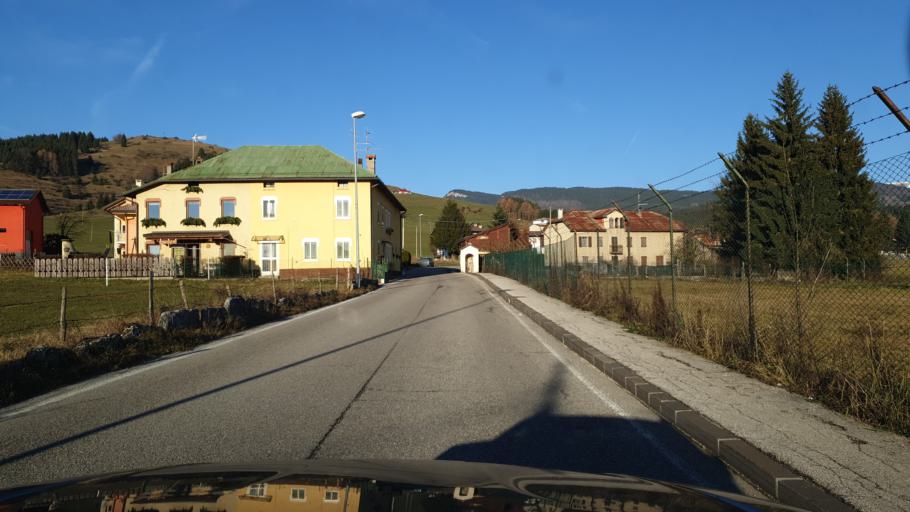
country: IT
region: Veneto
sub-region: Provincia di Vicenza
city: Asiago
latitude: 45.8858
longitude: 11.5084
